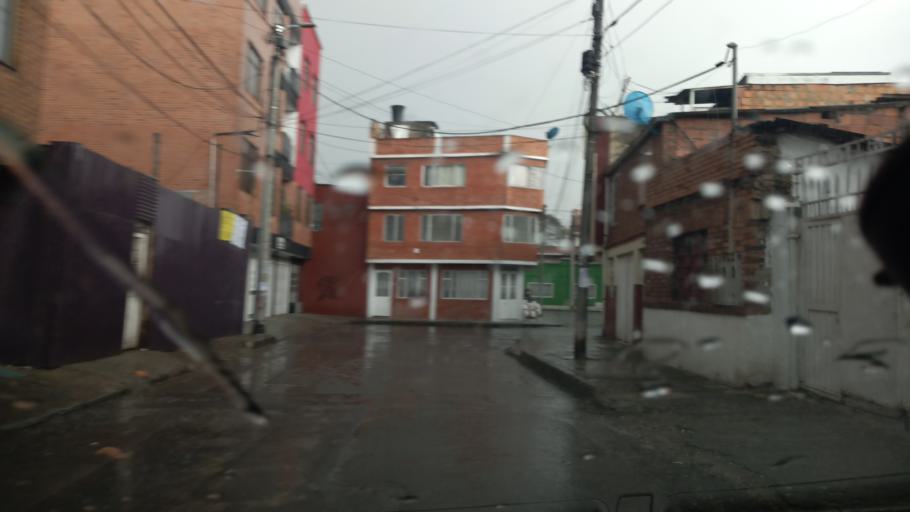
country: CO
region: Bogota D.C.
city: Bogota
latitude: 4.6728
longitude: -74.1384
